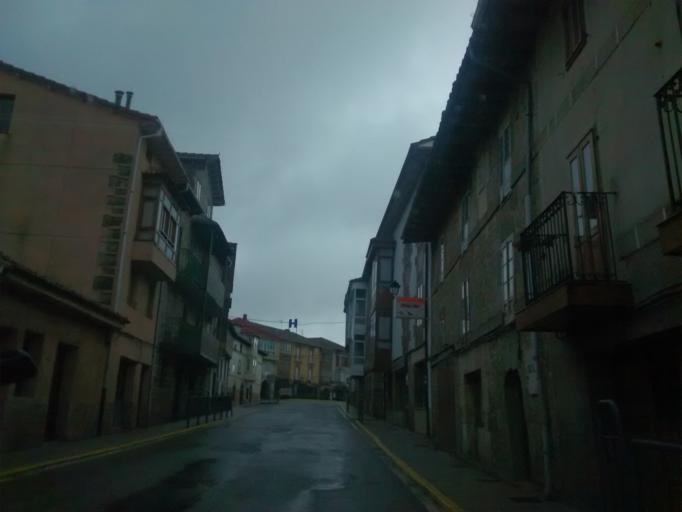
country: ES
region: Cantabria
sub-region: Provincia de Cantabria
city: San Pedro del Romeral
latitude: 42.9705
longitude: -3.7873
